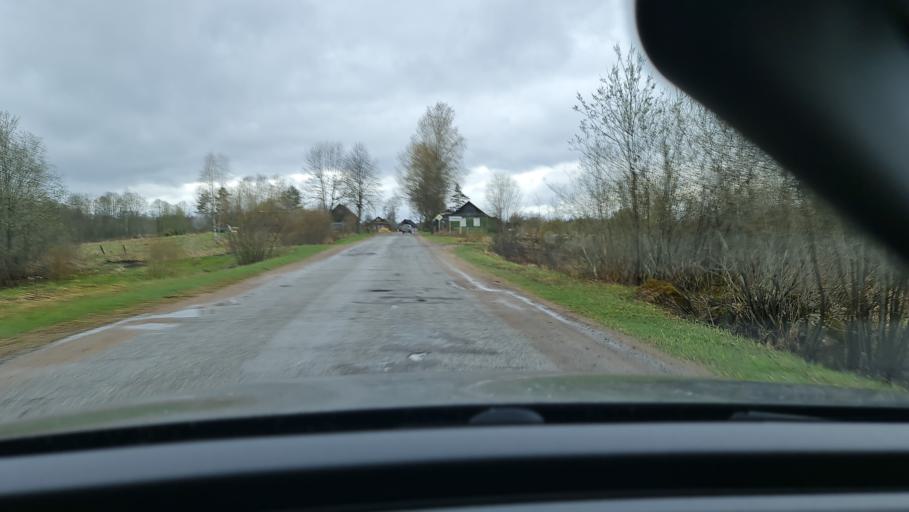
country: RU
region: Novgorod
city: Marevo
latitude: 57.2428
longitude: 32.0502
